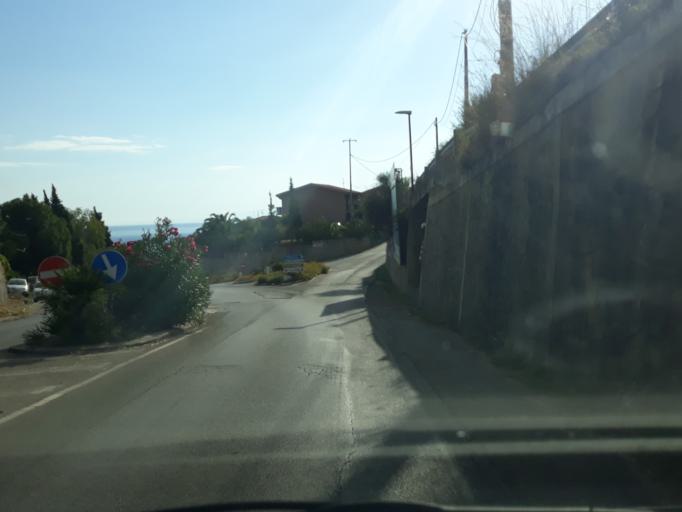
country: IT
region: Sicily
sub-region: Palermo
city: Cefalu
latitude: 38.0326
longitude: 14.0341
